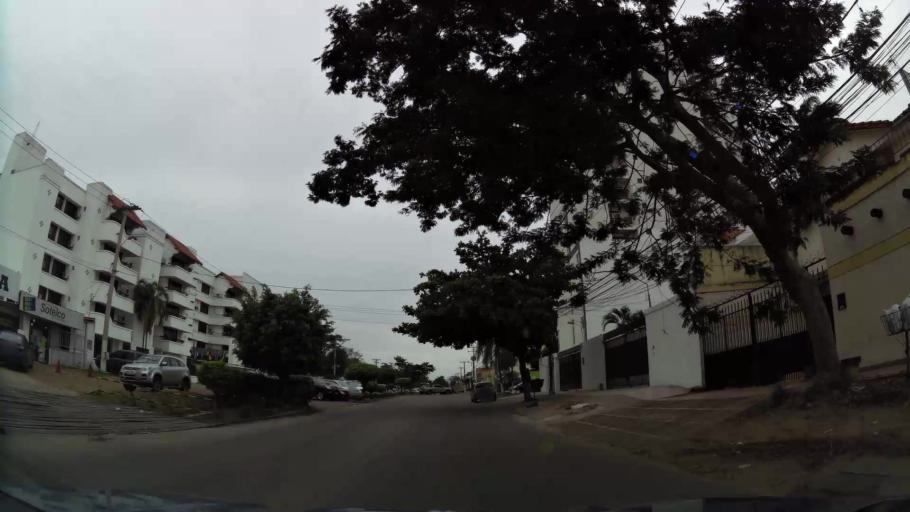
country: BO
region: Santa Cruz
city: Santa Cruz de la Sierra
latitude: -17.7616
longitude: -63.1941
